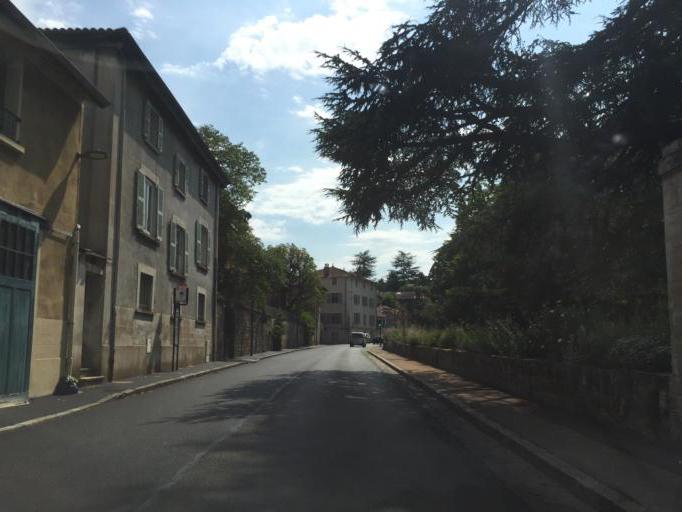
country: FR
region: Rhone-Alpes
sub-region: Departement du Rhone
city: Ecully
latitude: 45.7725
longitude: 4.7778
